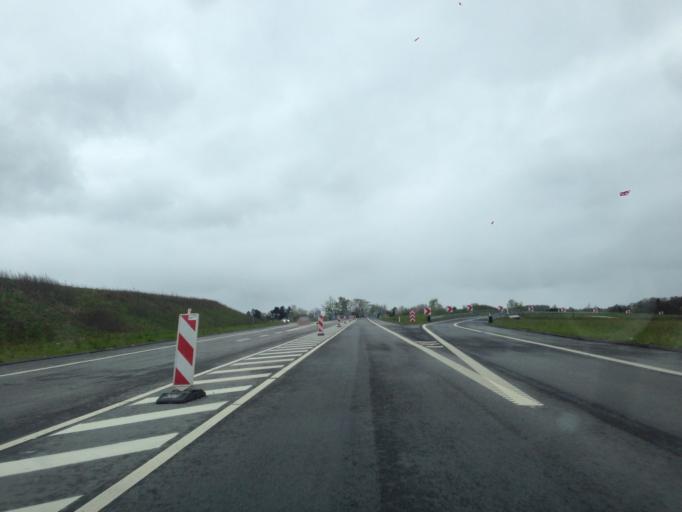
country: DK
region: Capital Region
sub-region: Rudersdal Kommune
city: Trorod
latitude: 55.8426
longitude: 12.5168
